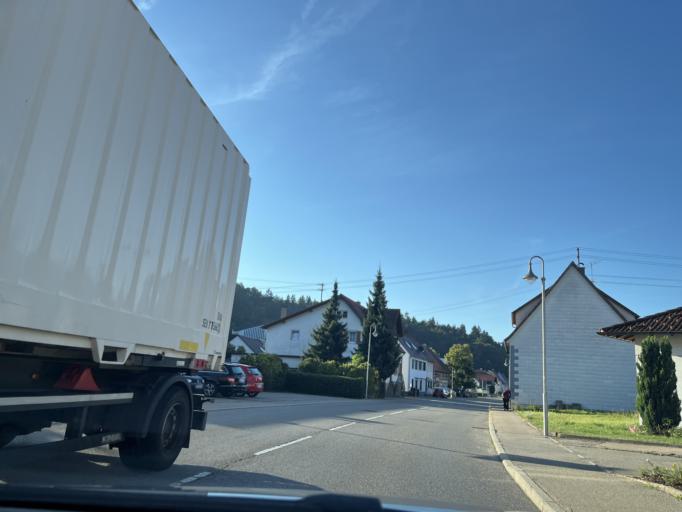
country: DE
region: Baden-Wuerttemberg
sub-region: Tuebingen Region
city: Neufra
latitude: 48.2753
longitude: 9.1679
